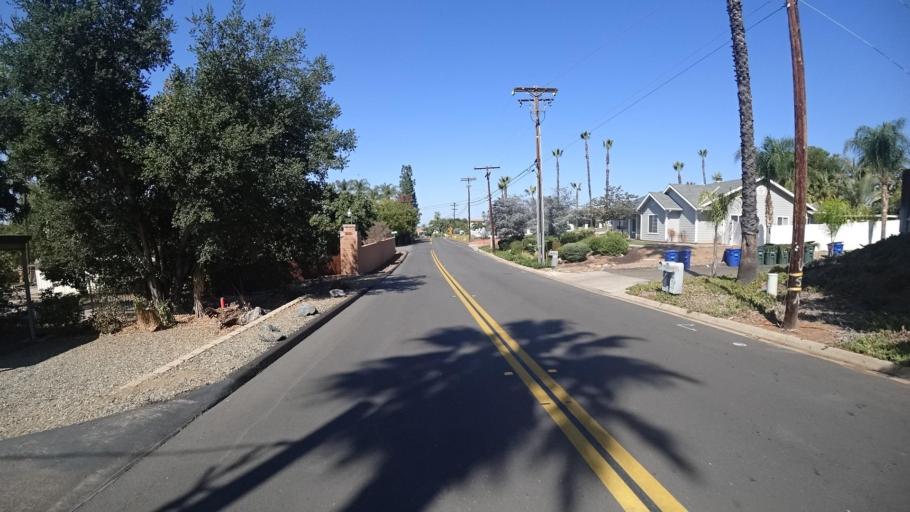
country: US
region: California
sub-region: San Diego County
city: Granite Hills
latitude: 32.7946
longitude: -116.9048
